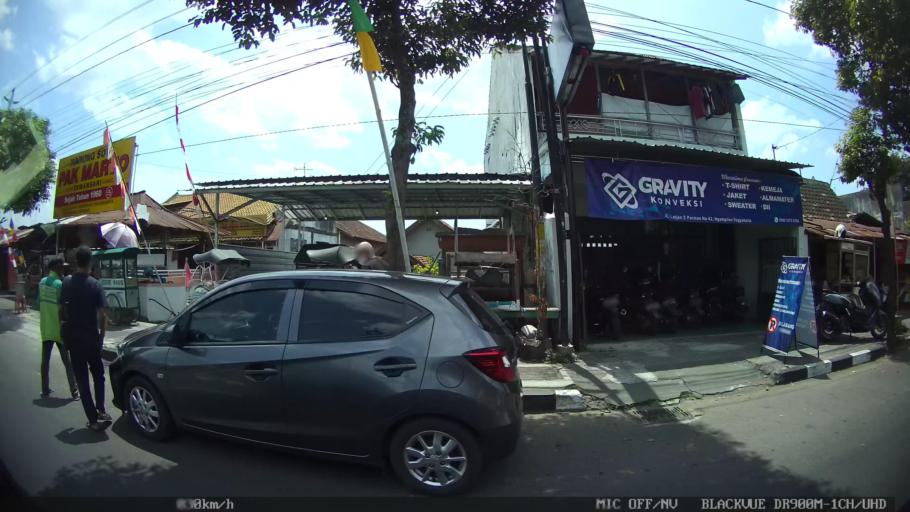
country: ID
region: Daerah Istimewa Yogyakarta
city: Yogyakarta
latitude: -7.8084
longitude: 110.3545
